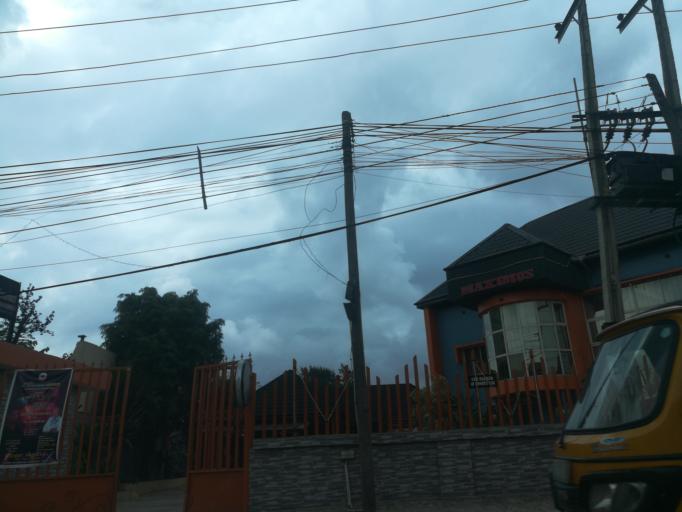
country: NG
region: Lagos
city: Ikeja
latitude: 6.6061
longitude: 3.3394
